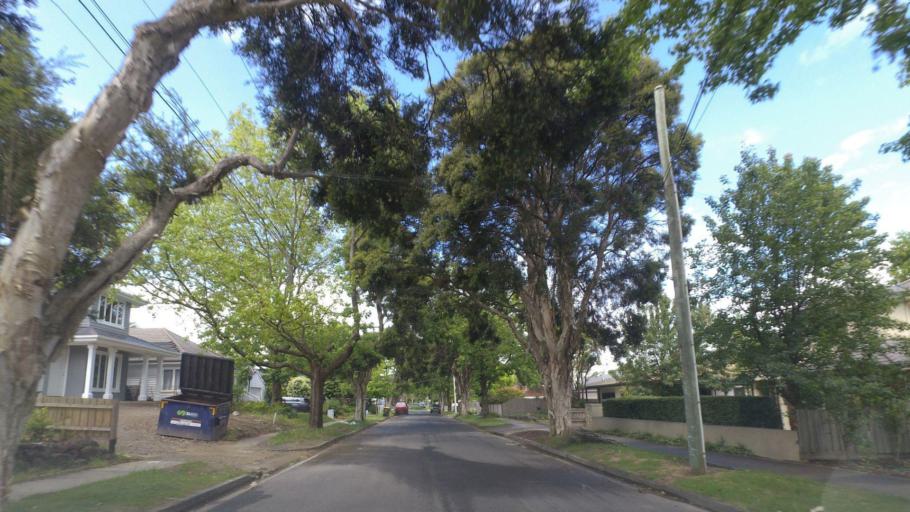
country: AU
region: Victoria
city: Forest Hill
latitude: -37.8260
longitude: 145.1896
